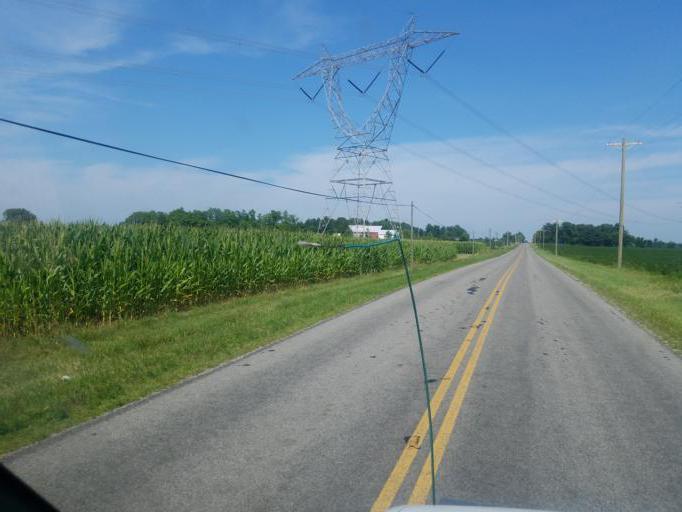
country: US
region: Ohio
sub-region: Shelby County
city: Jackson Center
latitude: 40.4977
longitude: -84.0710
